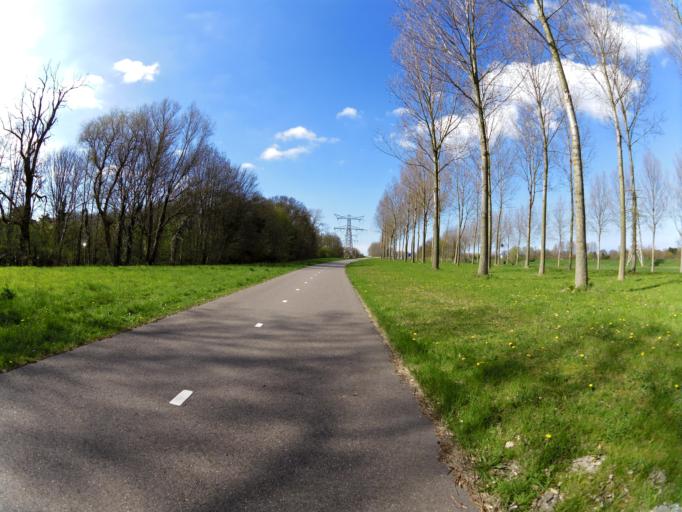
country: NL
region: South Holland
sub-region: Gemeente Brielle
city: Brielle
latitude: 51.9190
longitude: 4.1064
